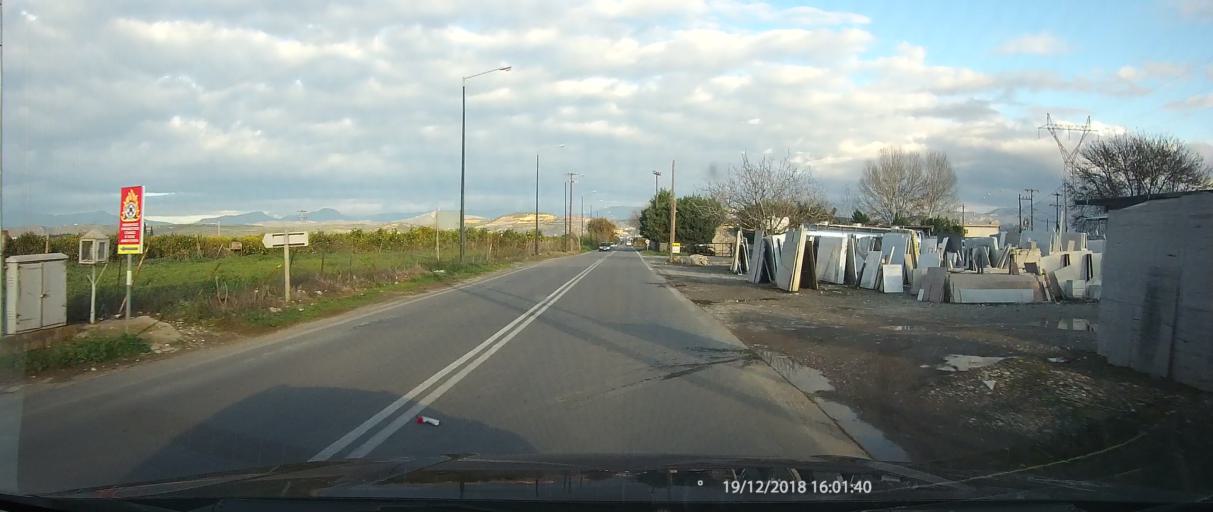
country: GR
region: Peloponnese
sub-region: Nomos Lakonias
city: Vlakhiotis
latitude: 36.8574
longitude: 22.6909
